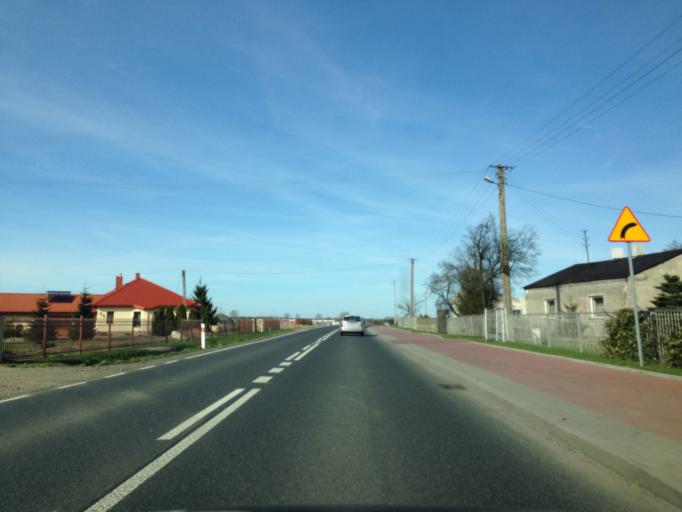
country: PL
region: Lodz Voivodeship
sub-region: Powiat poddebicki
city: Wartkowice
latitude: 51.9889
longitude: 19.0371
